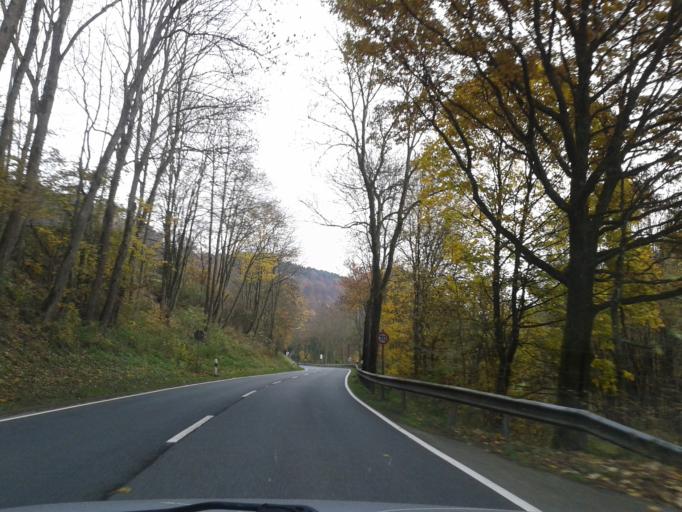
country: DE
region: North Rhine-Westphalia
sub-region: Regierungsbezirk Arnsberg
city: Bad Laasphe
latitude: 50.9317
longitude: 8.3874
